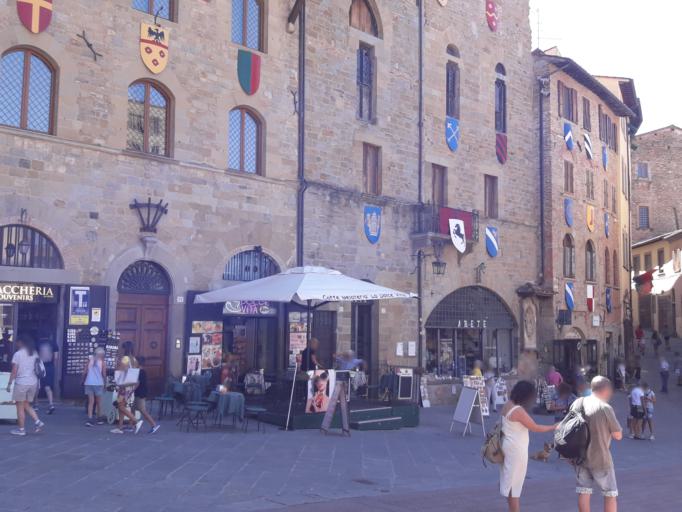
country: IT
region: Tuscany
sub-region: Province of Arezzo
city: Arezzo
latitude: 43.4646
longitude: 11.8846
